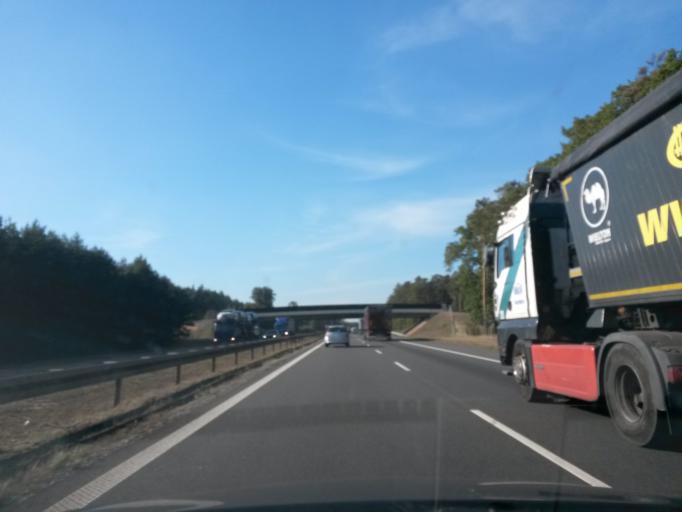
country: PL
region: Opole Voivodeship
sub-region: Powiat opolski
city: Komprachcice
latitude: 50.5924
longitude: 17.8066
